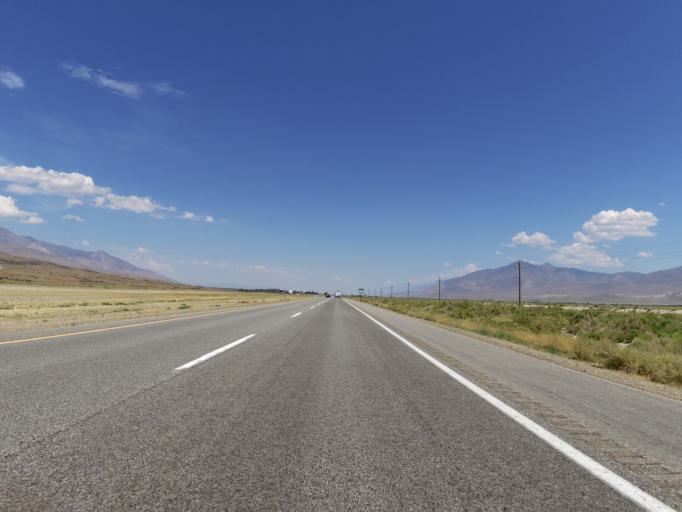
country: US
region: California
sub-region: Inyo County
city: Big Pine
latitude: 37.0974
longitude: -118.2500
